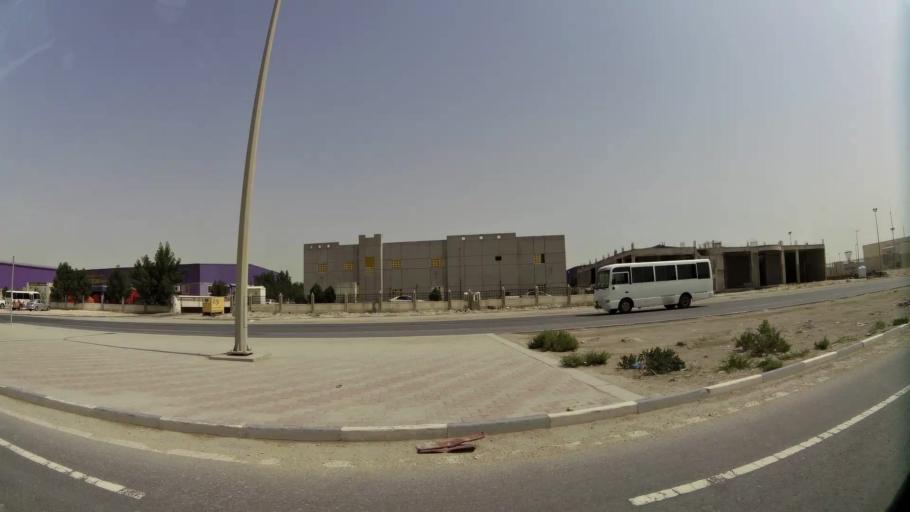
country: QA
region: Al Wakrah
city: Al Wukayr
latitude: 25.1611
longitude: 51.4072
